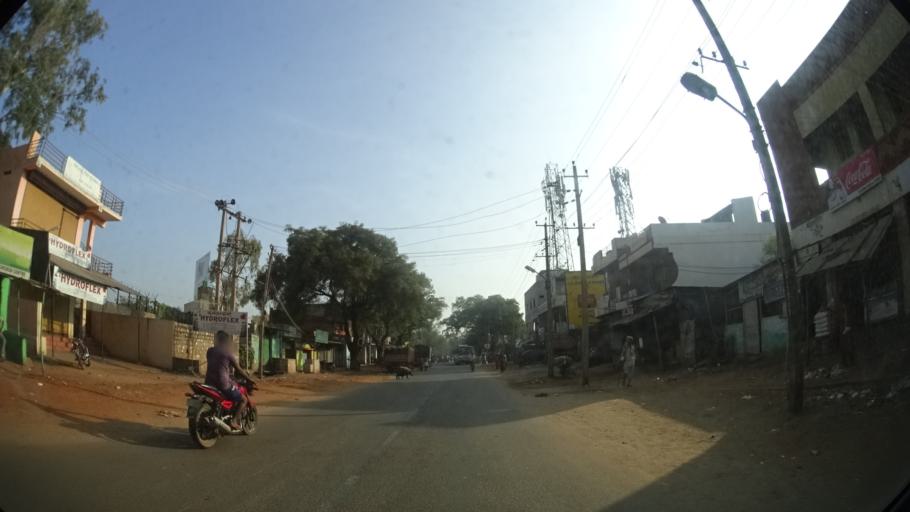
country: IN
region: Karnataka
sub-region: Bellary
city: Hospet
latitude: 15.2613
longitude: 76.3812
